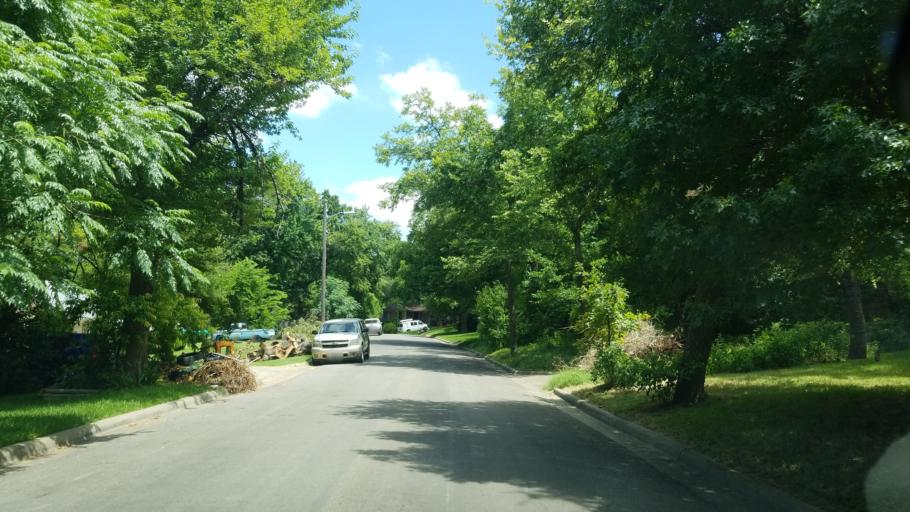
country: US
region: Texas
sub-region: Dallas County
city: Balch Springs
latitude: 32.7561
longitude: -96.6961
